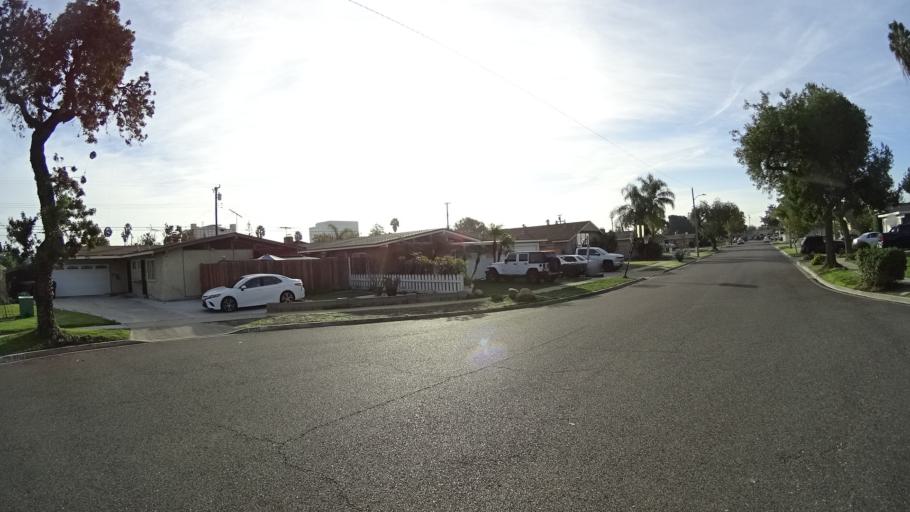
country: US
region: California
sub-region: Orange County
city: Garden Grove
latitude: 33.7925
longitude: -117.9219
